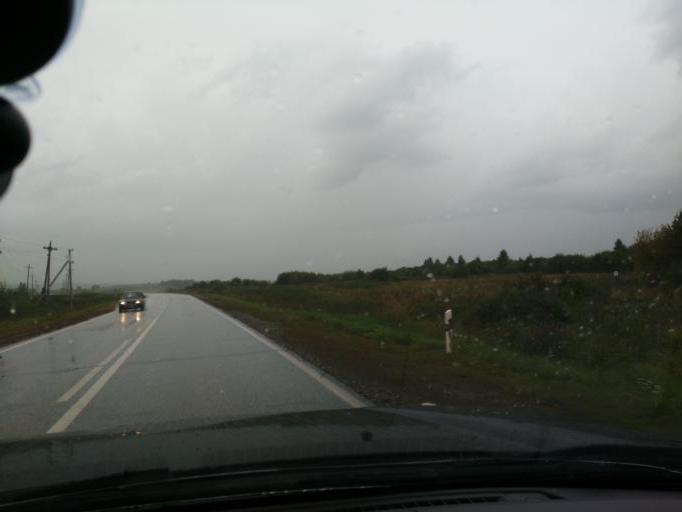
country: RU
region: Perm
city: Barda
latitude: 57.0814
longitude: 55.5427
